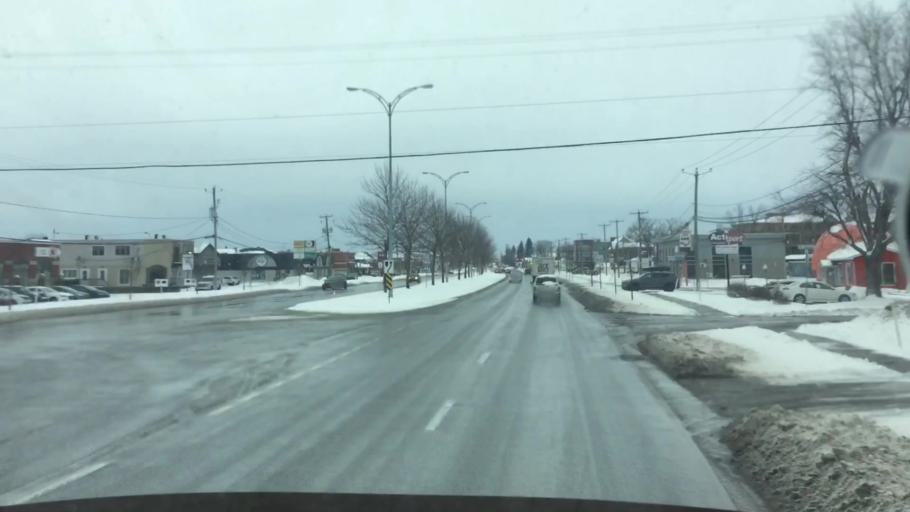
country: CA
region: Quebec
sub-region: Monteregie
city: Saint-Jean-sur-Richelieu
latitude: 45.3535
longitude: -73.2947
